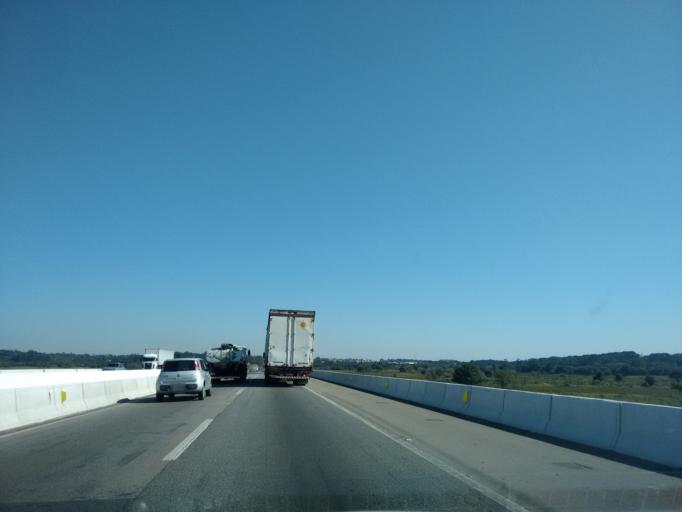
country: BR
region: Parana
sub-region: Sao Jose Dos Pinhais
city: Sao Jose dos Pinhais
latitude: -25.5687
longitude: -49.2287
